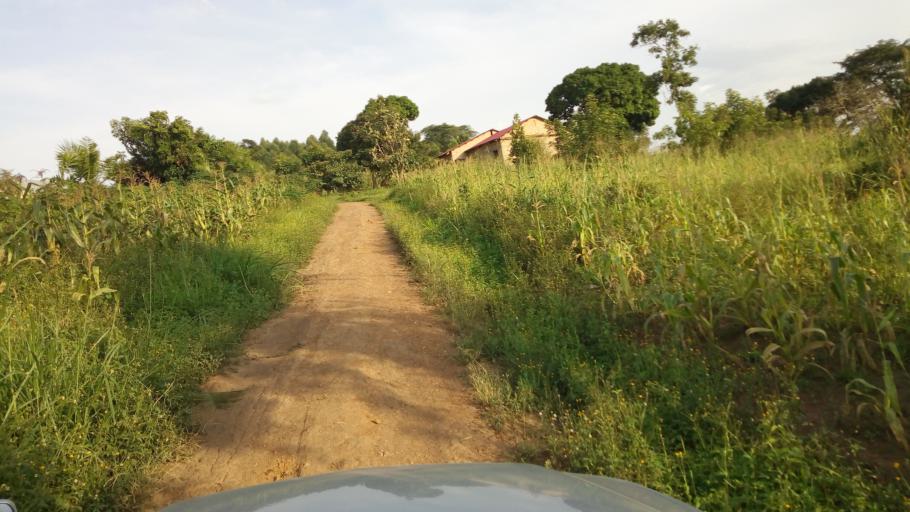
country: UG
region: Central Region
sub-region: Kiboga District
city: Kiboga
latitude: 0.7263
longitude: 31.7368
